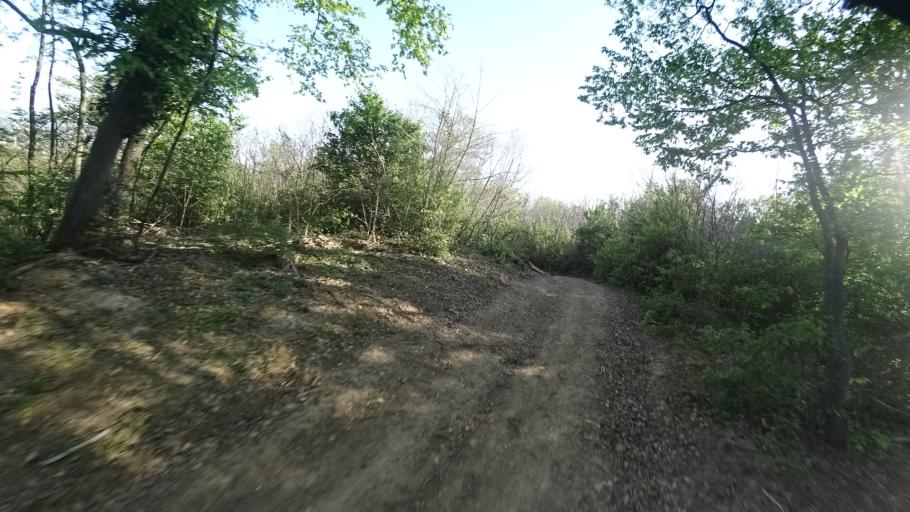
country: HR
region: Grad Zagreb
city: Stenjevec
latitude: 45.8511
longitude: 15.9129
